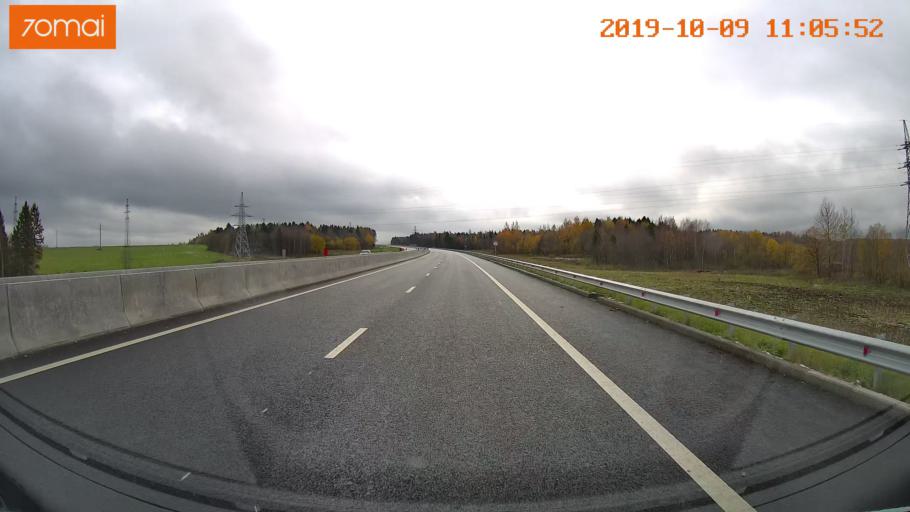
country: RU
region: Vologda
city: Molochnoye
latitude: 59.1939
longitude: 39.7581
